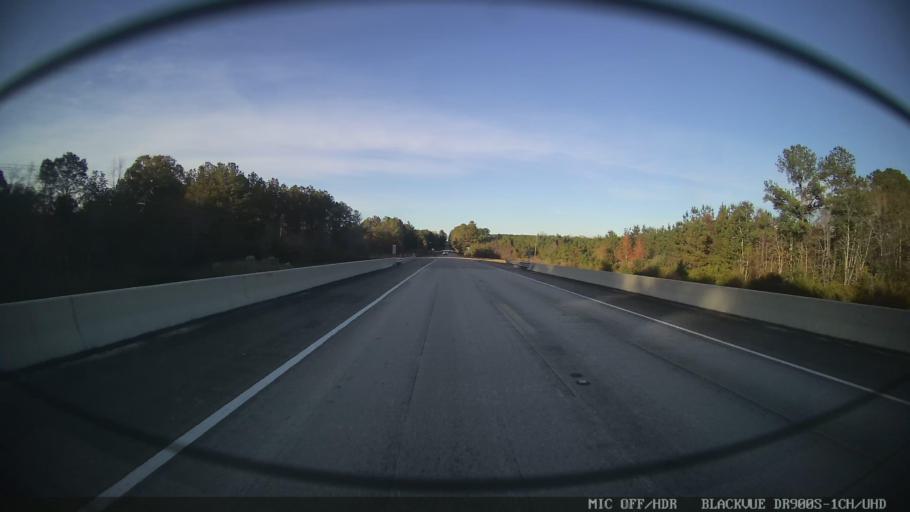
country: US
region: Mississippi
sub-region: Lamar County
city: Purvis
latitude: 31.0857
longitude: -89.4166
